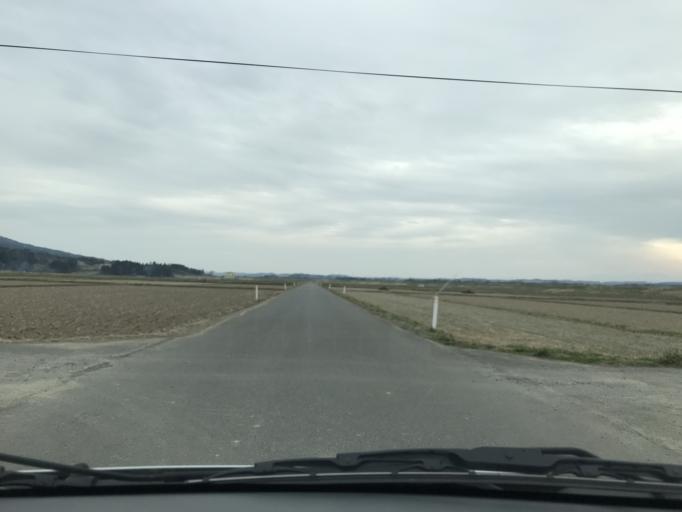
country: JP
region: Iwate
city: Mizusawa
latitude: 39.0574
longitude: 141.1661
